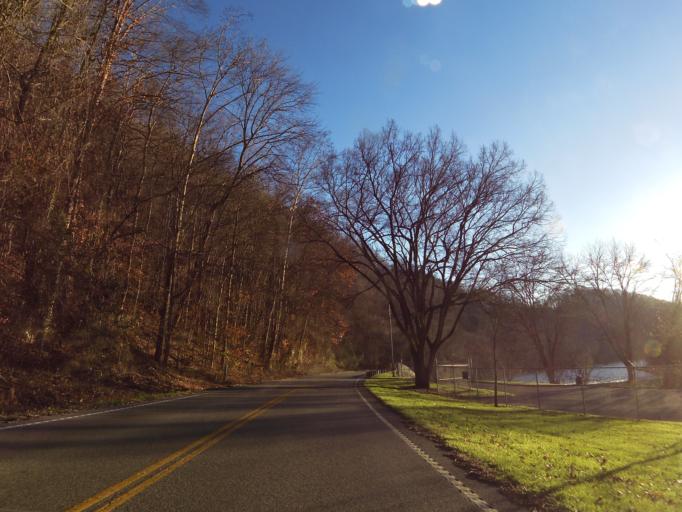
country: US
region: Tennessee
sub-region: Anderson County
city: Norris
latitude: 36.2107
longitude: -84.0732
